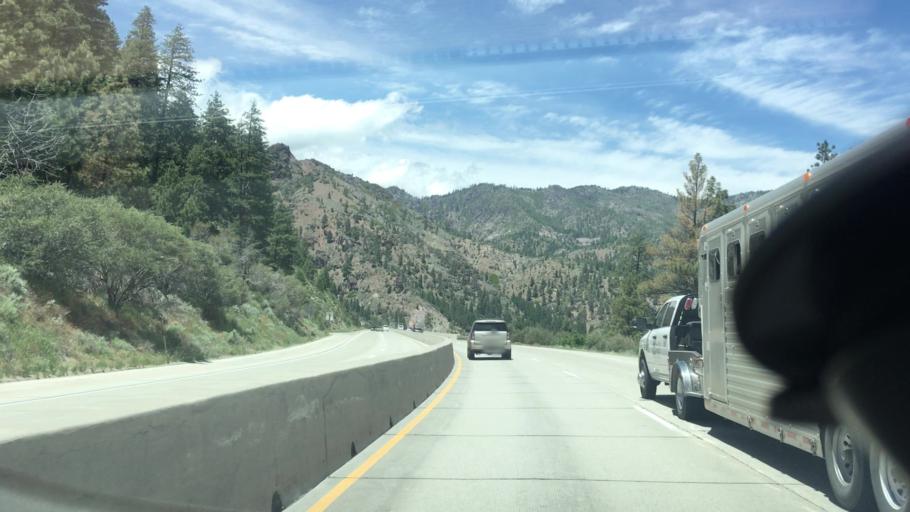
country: US
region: Nevada
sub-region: Washoe County
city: Verdi
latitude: 39.4157
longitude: -120.0291
